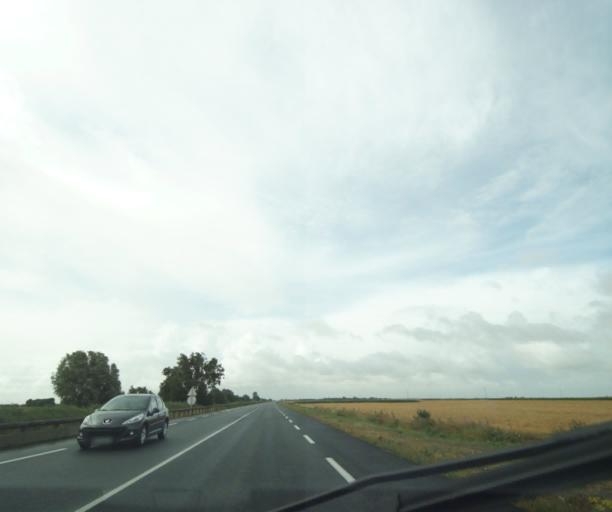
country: FR
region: Pays de la Loire
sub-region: Departement de la Vendee
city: Champagne-les-Marais
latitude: 46.3706
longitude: -1.0894
